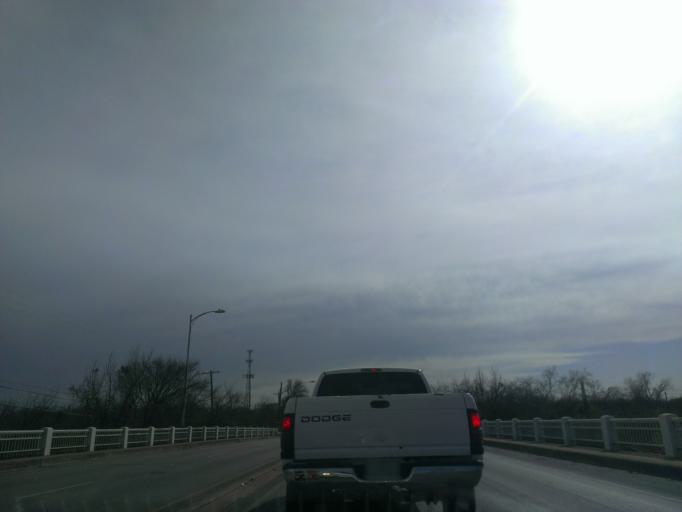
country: US
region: Texas
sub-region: Travis County
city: Austin
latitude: 30.2621
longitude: -97.6945
